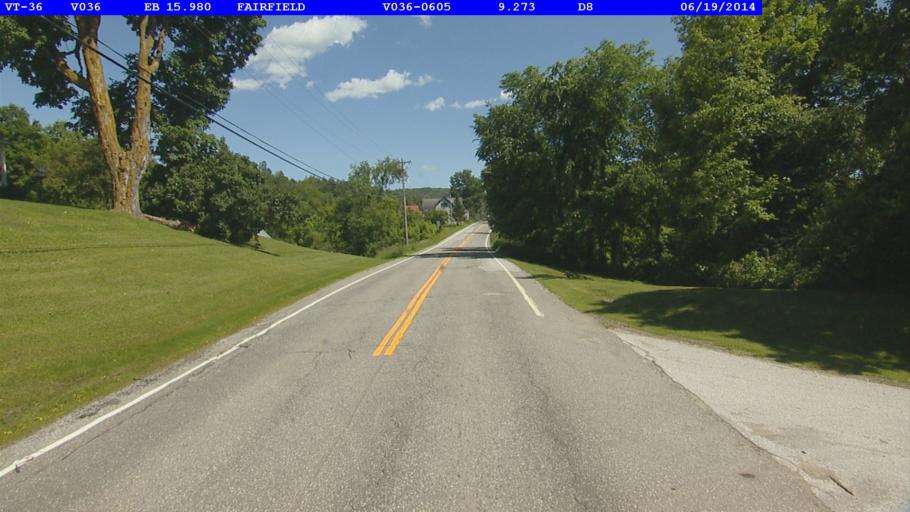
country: US
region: Vermont
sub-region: Franklin County
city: Enosburg Falls
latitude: 44.7866
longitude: -72.8617
